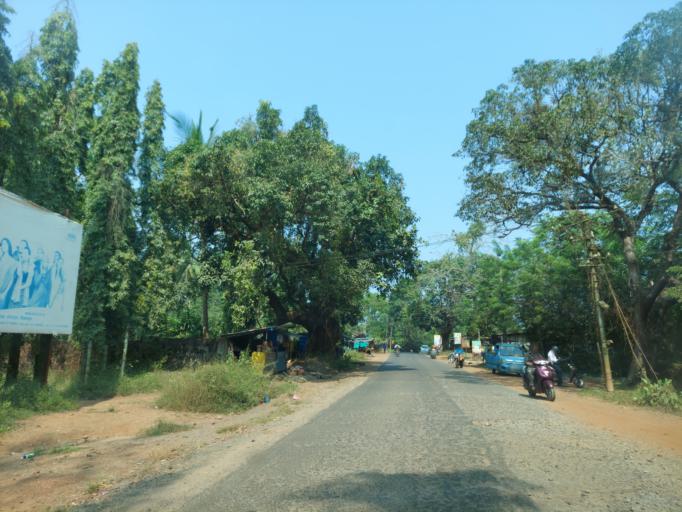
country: IN
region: Maharashtra
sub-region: Sindhudurg
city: Kudal
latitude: 15.9990
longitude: 73.6856
